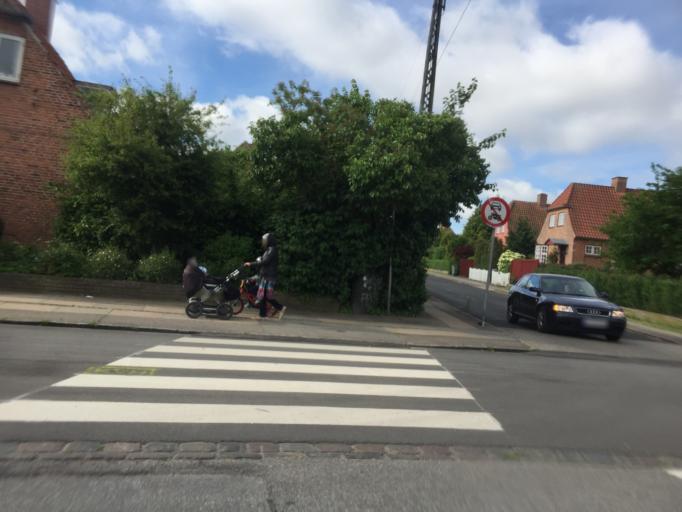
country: DK
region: Capital Region
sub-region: Frederiksberg Kommune
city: Frederiksberg
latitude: 55.6962
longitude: 12.5166
